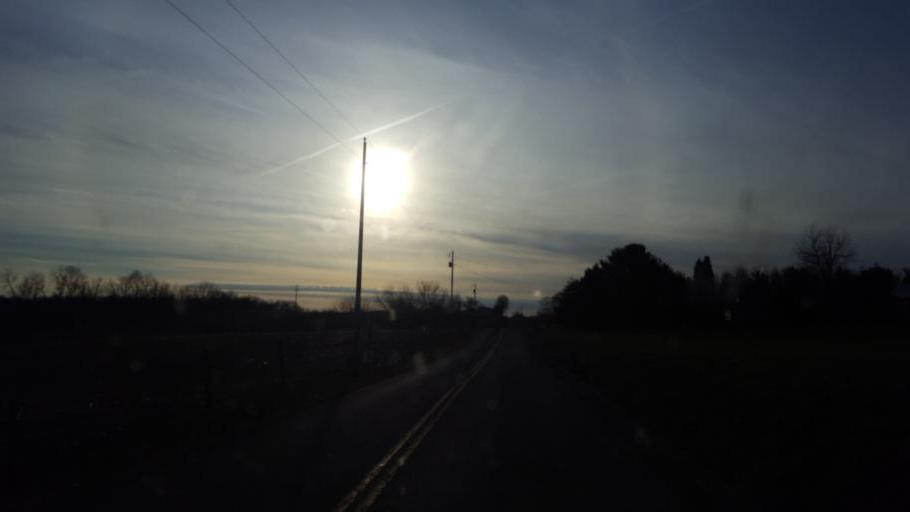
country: US
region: Ohio
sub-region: Sandusky County
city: Bellville
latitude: 40.5382
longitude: -82.4218
